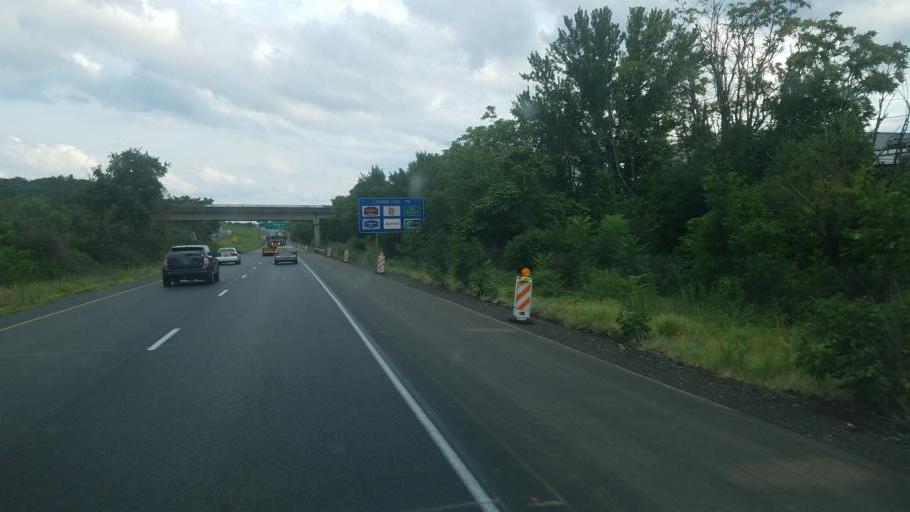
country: US
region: Pennsylvania
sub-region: Butler County
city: Fox Run
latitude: 40.7053
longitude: -80.1018
